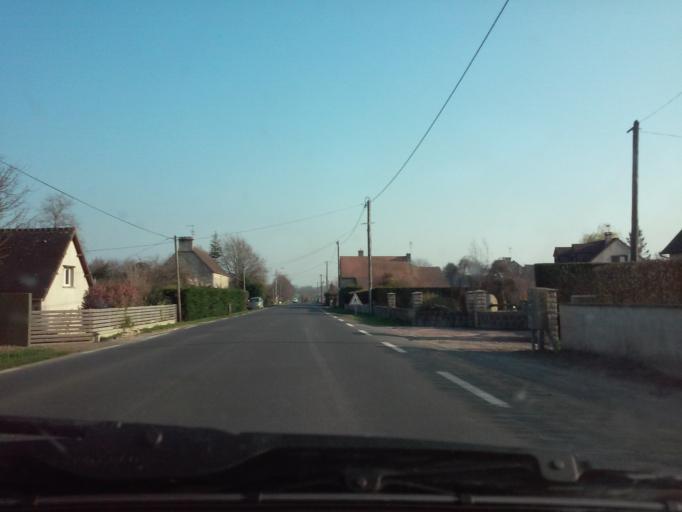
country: FR
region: Lower Normandy
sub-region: Departement du Calvados
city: Tilly-sur-Seulles
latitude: 49.1929
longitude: -0.6415
